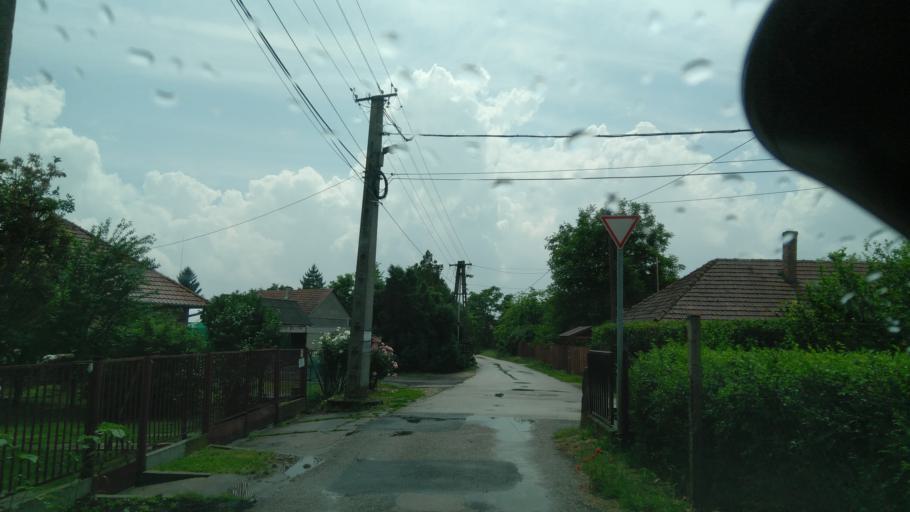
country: HU
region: Bekes
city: Bekescsaba
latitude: 46.6646
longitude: 21.1738
